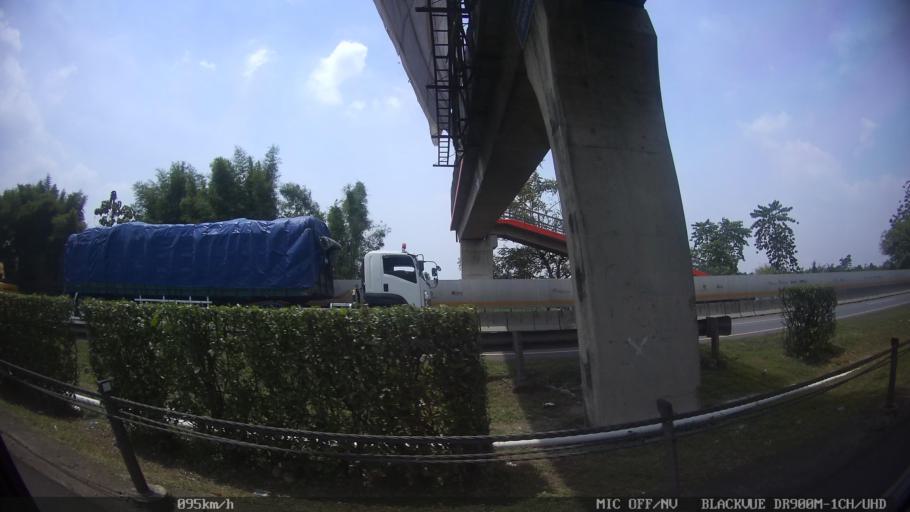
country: ID
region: Banten
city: Serang
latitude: -6.1371
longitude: 106.2177
